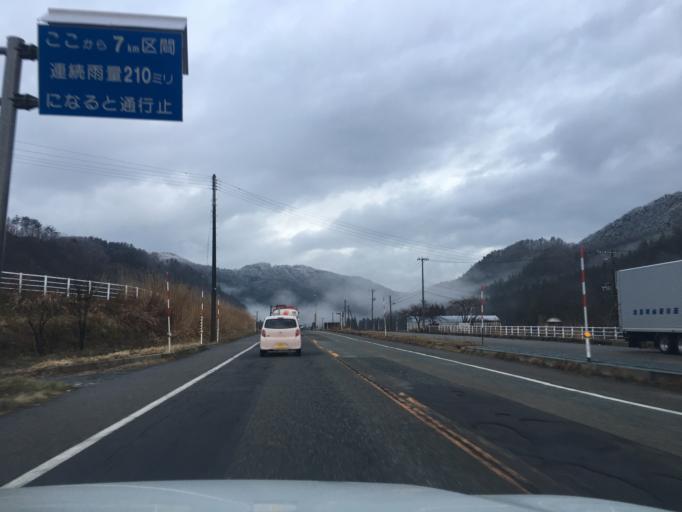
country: JP
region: Niigata
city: Murakami
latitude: 38.4427
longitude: 139.5871
